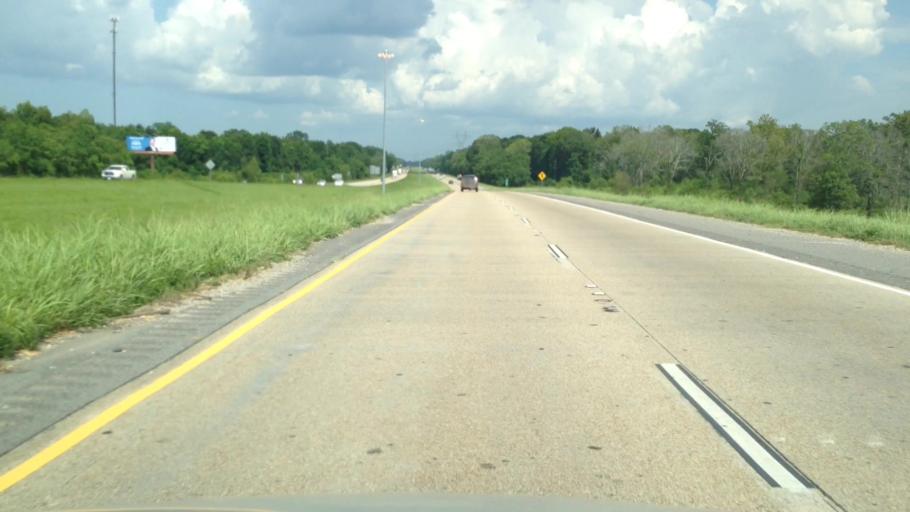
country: US
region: Louisiana
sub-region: Ascension Parish
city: Sorrento
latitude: 30.1712
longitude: -90.8759
